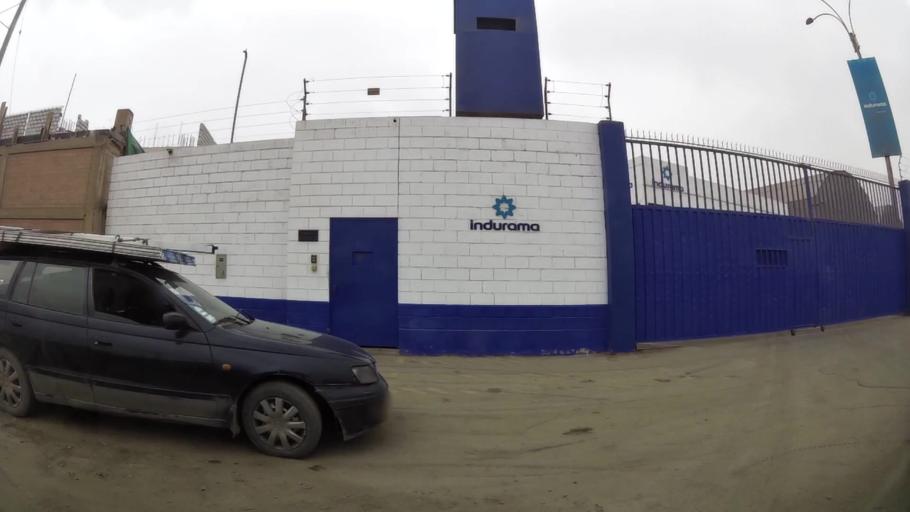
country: PE
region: Lima
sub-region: Lima
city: Punta Hermosa
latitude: -12.2918
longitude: -76.8348
